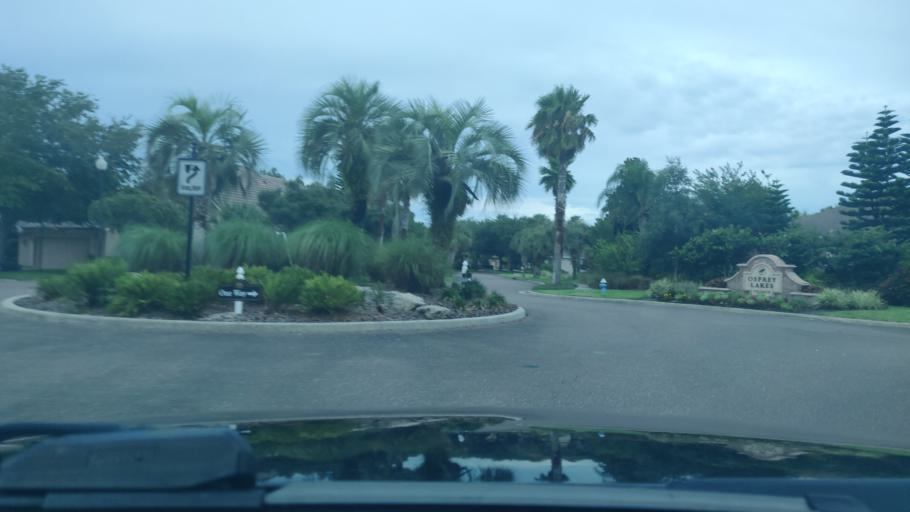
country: US
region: Florida
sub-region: Flagler County
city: Palm Coast
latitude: 29.5330
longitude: -81.1652
